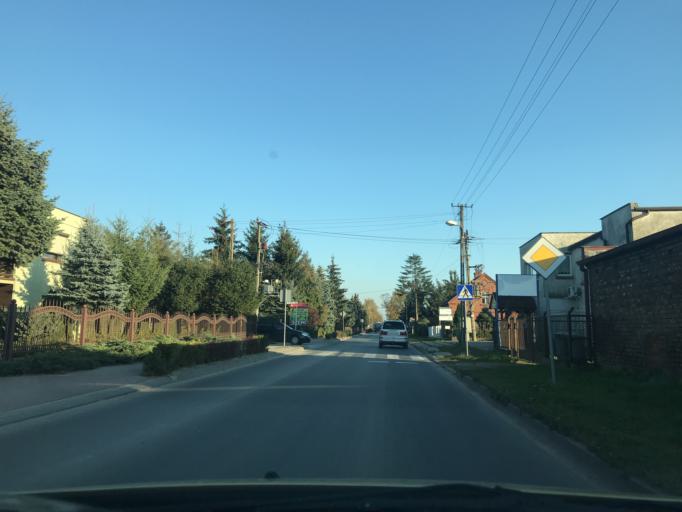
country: PL
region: Greater Poland Voivodeship
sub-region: Powiat poznanski
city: Baranowo
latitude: 52.3987
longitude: 16.7517
